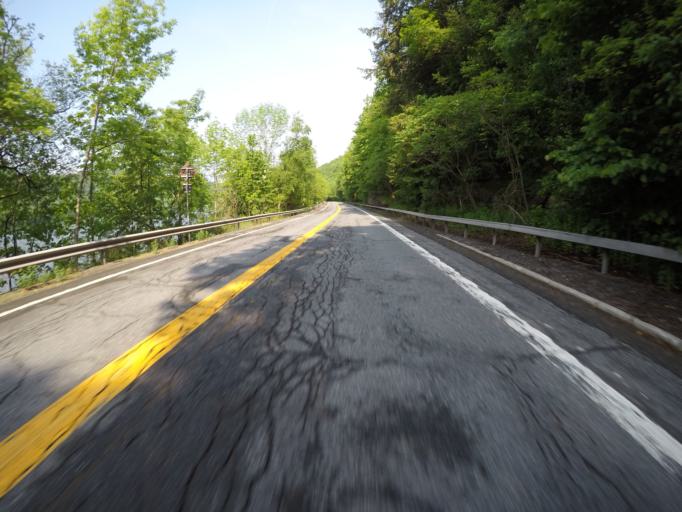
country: US
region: New York
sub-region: Sullivan County
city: Livingston Manor
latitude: 42.0893
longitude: -74.8040
